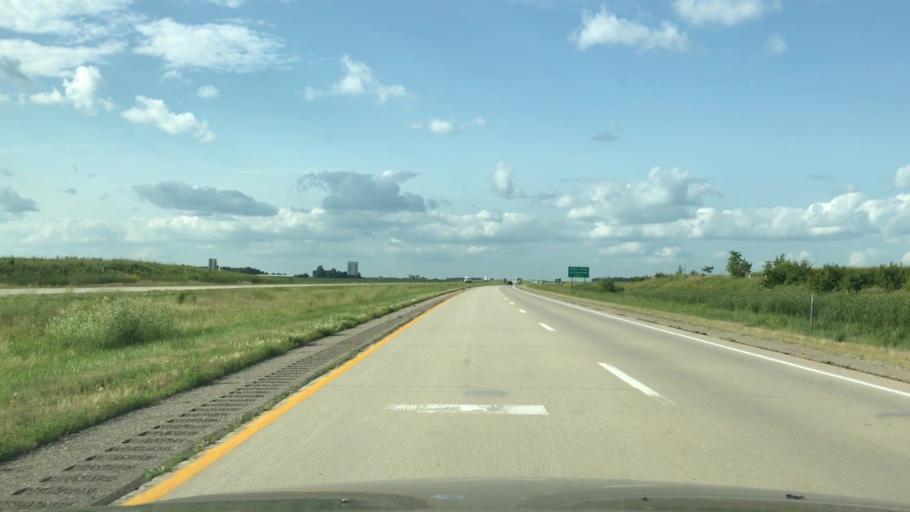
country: US
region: Iowa
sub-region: Osceola County
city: Sibley
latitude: 43.4193
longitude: -95.7166
